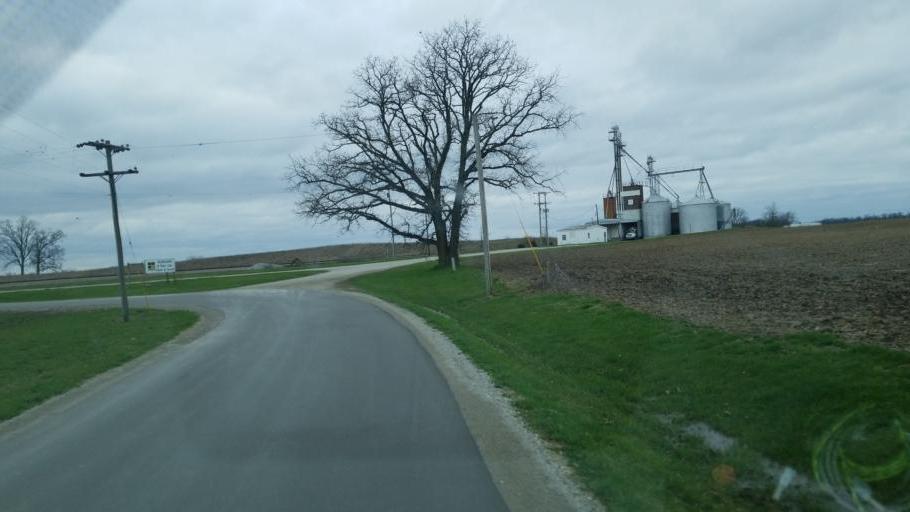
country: US
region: Ohio
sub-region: Fayette County
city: Jeffersonville
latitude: 39.5883
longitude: -83.5147
